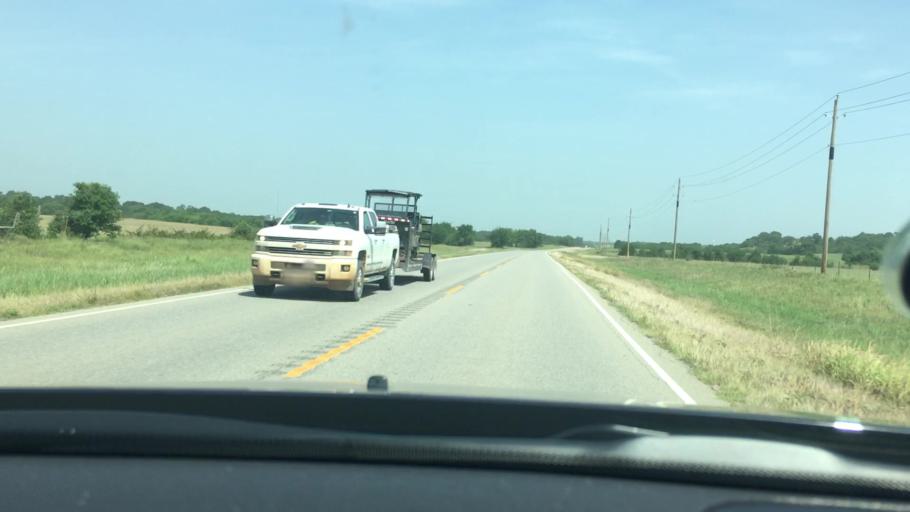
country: US
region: Oklahoma
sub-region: Atoka County
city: Atoka
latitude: 34.4339
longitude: -96.1995
